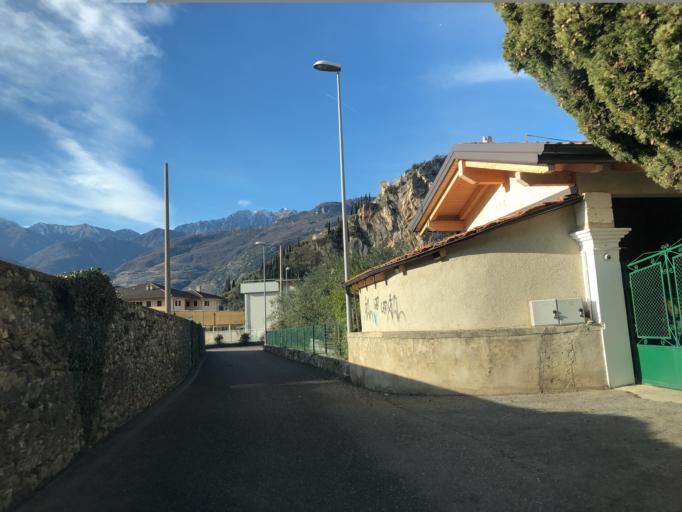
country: IT
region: Trentino-Alto Adige
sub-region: Provincia di Trento
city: Arco
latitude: 45.9189
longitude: 10.8951
